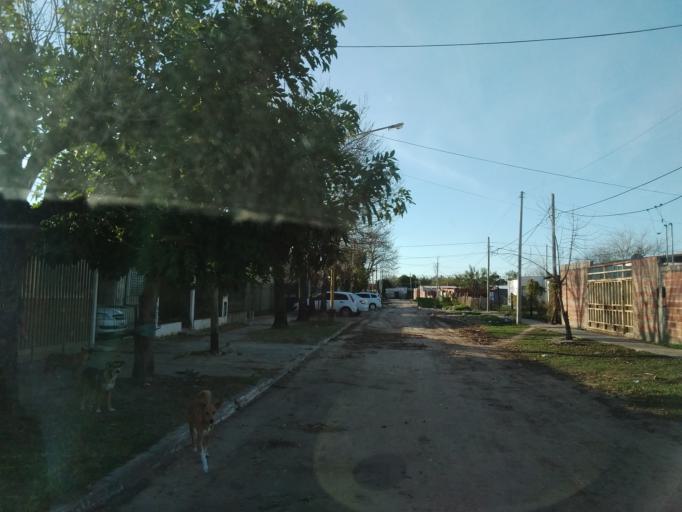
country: AR
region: Corrientes
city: Corrientes
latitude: -27.5029
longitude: -58.8301
